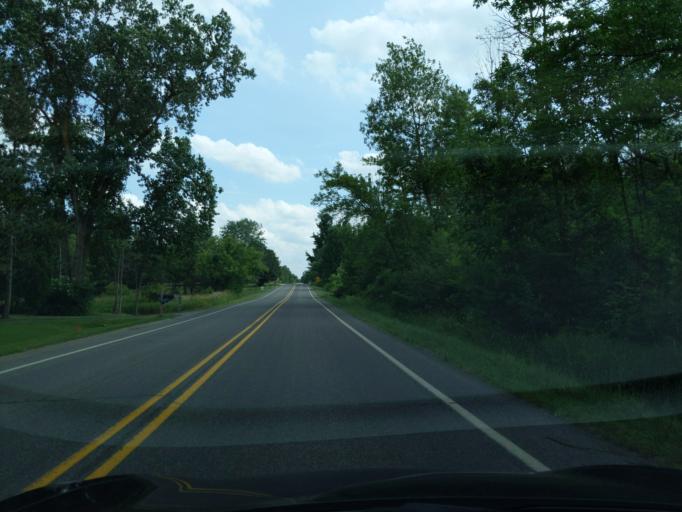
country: US
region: Michigan
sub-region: Eaton County
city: Dimondale
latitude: 42.5996
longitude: -84.6026
